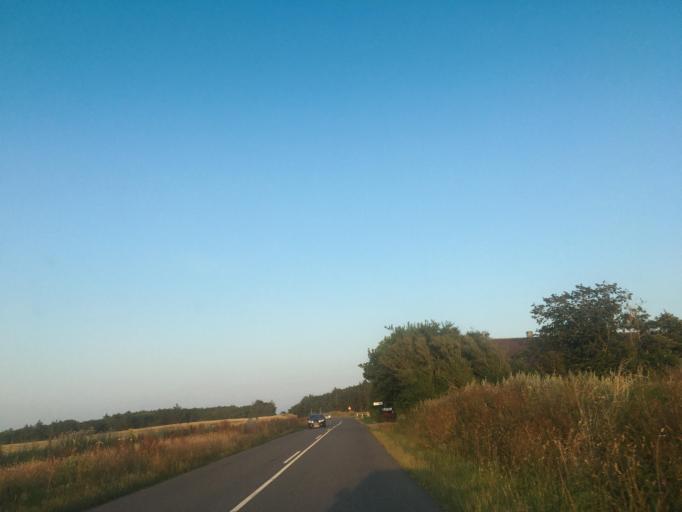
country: DK
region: North Denmark
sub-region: Thisted Kommune
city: Hurup
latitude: 56.7581
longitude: 8.3489
